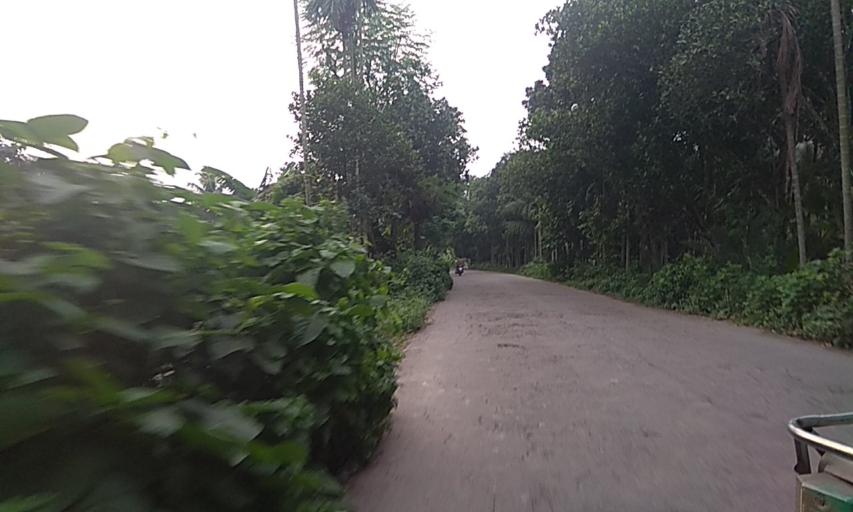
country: BD
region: Dhaka
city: Dohar
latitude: 23.4604
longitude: 89.9978
